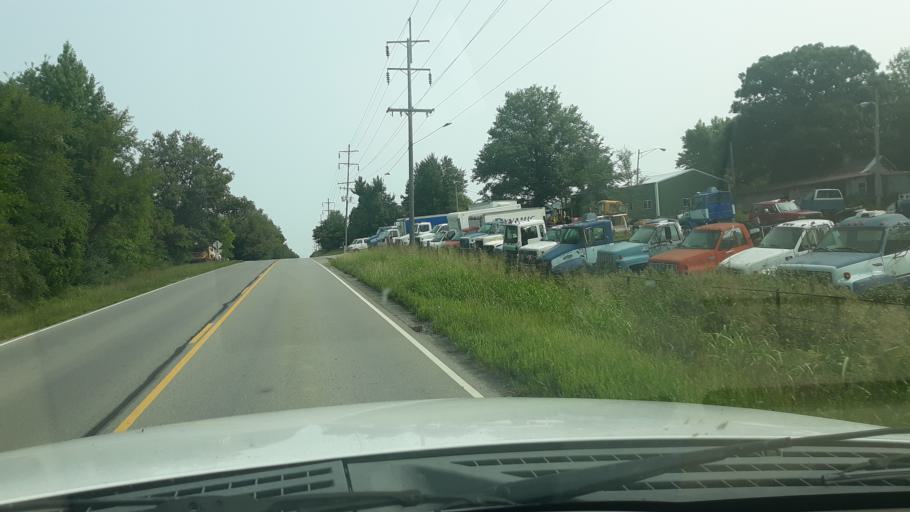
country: US
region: Illinois
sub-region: White County
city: Norris City
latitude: 37.9517
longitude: -88.3384
